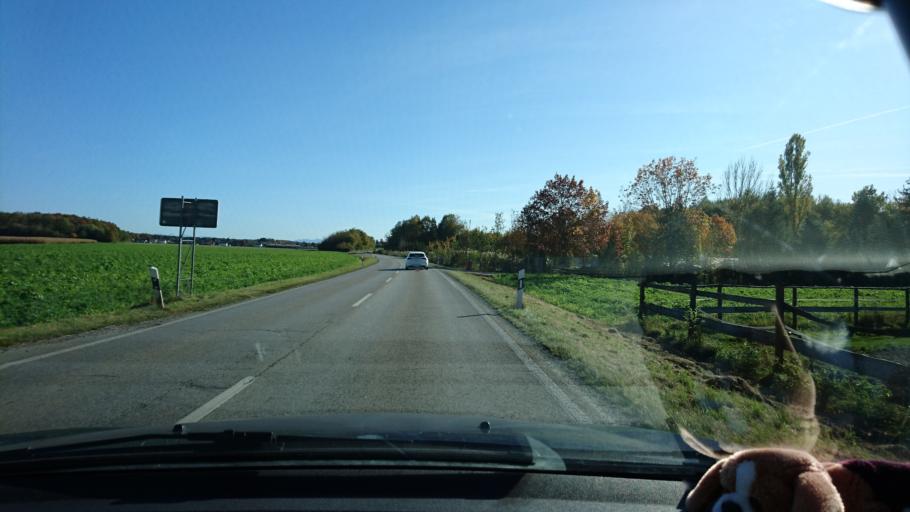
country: DE
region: Bavaria
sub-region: Upper Bavaria
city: Zorneding
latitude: 48.1075
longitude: 11.8297
